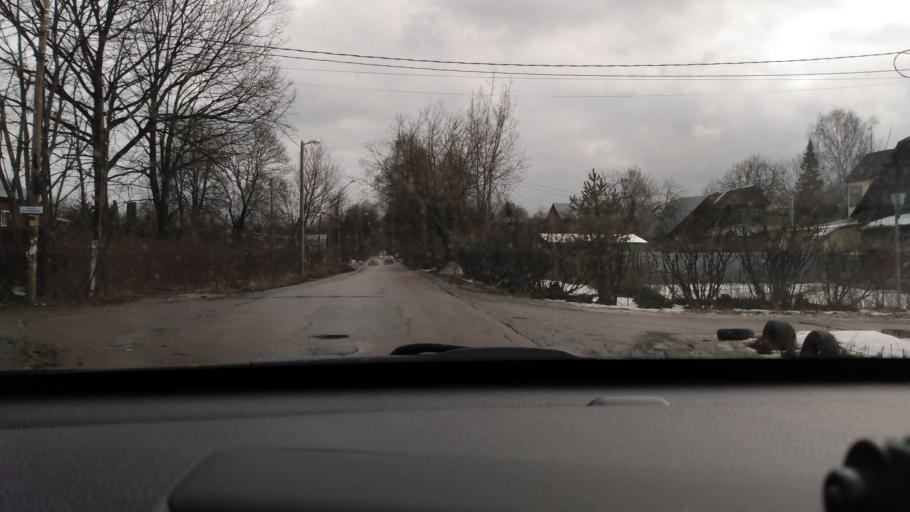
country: RU
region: Moskovskaya
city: Yubileyny
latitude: 55.9279
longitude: 37.8692
